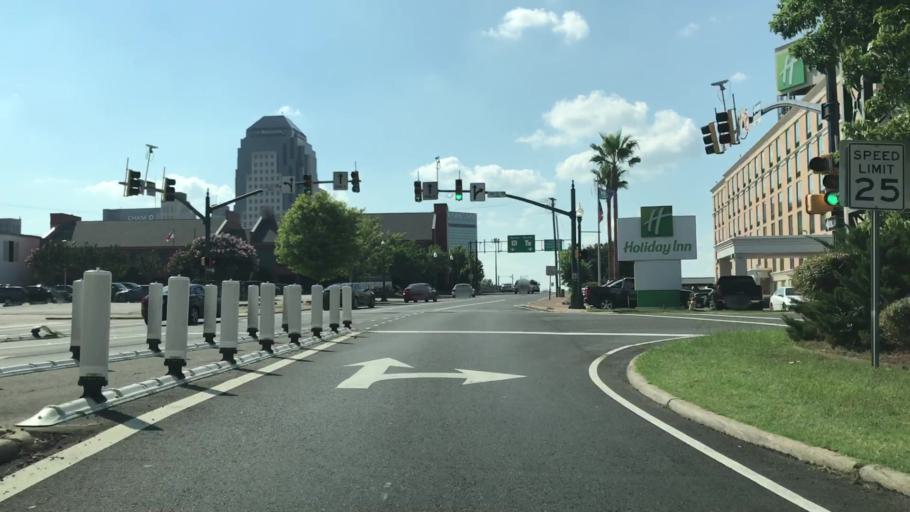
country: US
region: Louisiana
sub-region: Bossier Parish
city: Bossier City
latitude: 32.5116
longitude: -93.7432
